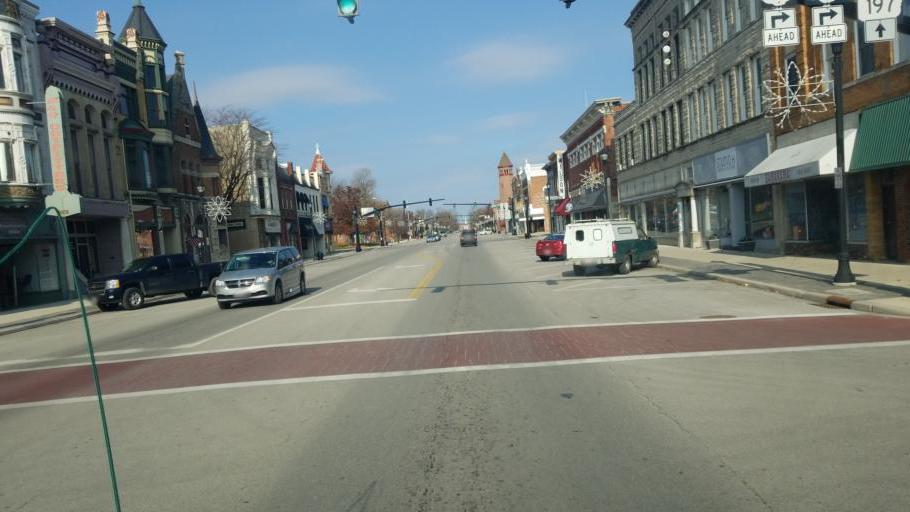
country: US
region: Ohio
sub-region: Mercer County
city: Celina
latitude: 40.5480
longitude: -84.5708
